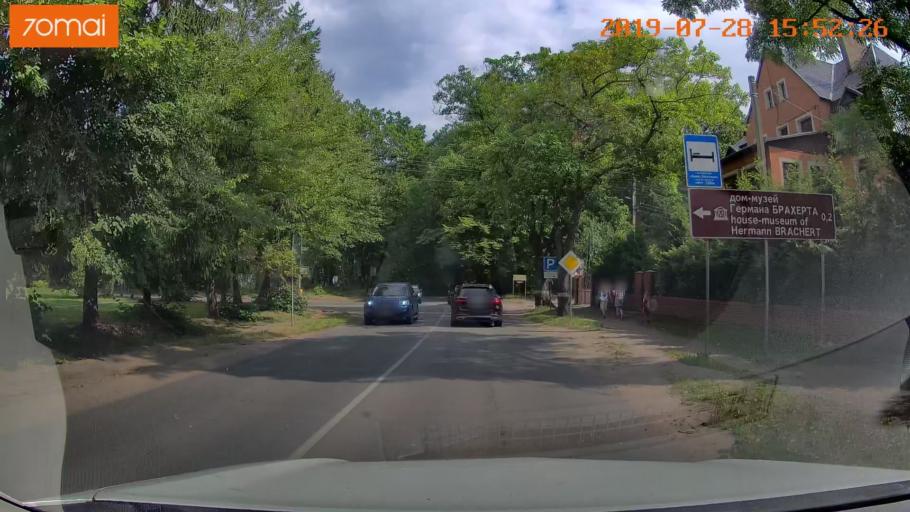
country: RU
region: Kaliningrad
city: Otradnoye
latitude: 54.9402
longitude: 20.1136
